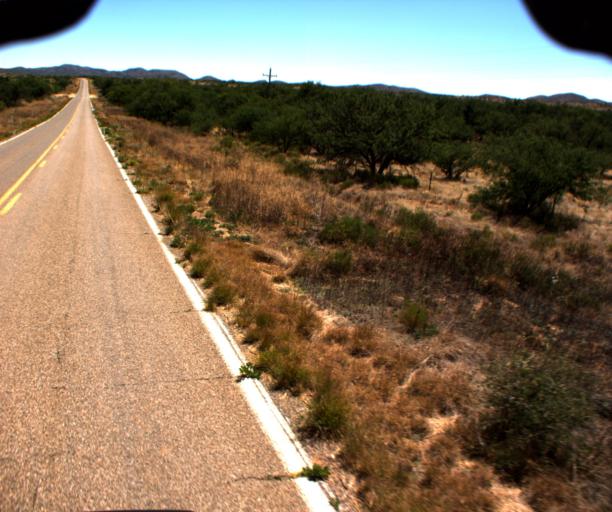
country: US
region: Arizona
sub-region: Santa Cruz County
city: Tubac
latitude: 31.5170
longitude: -111.5429
